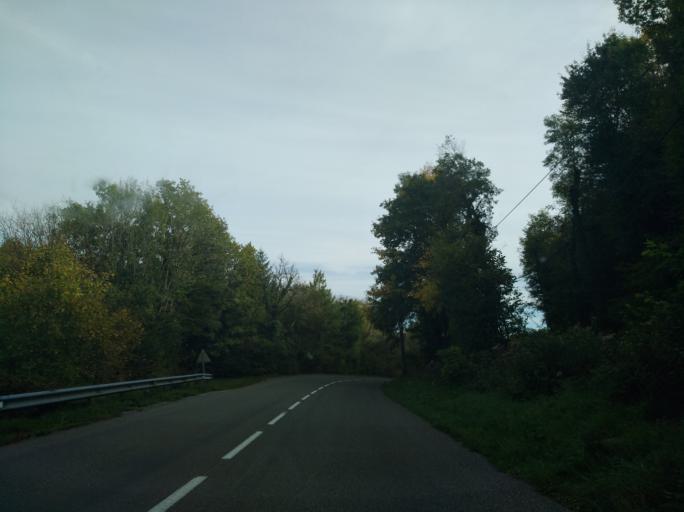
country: FR
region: Bourgogne
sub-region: Departement de Saone-et-Loire
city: Cuiseaux
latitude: 46.4615
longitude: 5.4024
